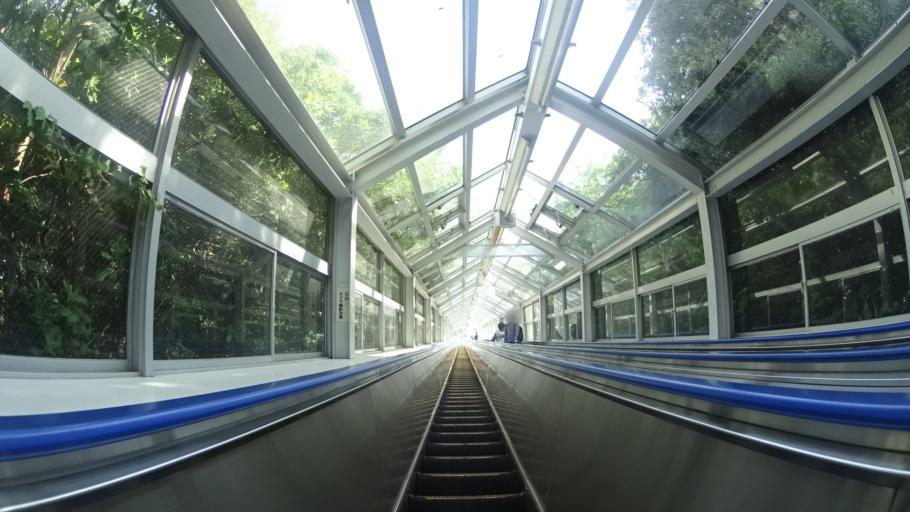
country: JP
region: Tokushima
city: Narutocho-mitsuishi
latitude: 34.2361
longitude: 134.6401
